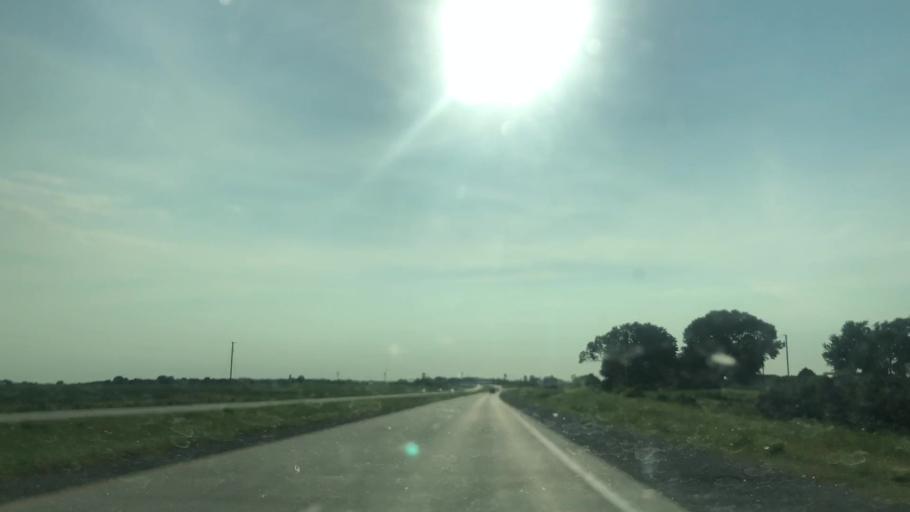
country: US
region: Iowa
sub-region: Story County
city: Nevada
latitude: 42.0081
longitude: -93.4180
